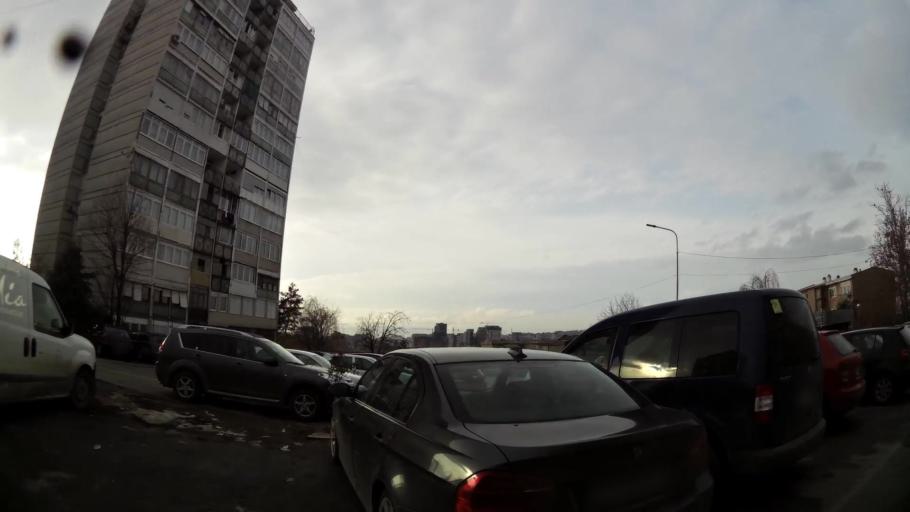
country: XK
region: Pristina
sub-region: Komuna e Prishtines
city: Pristina
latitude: 42.6515
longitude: 21.1627
